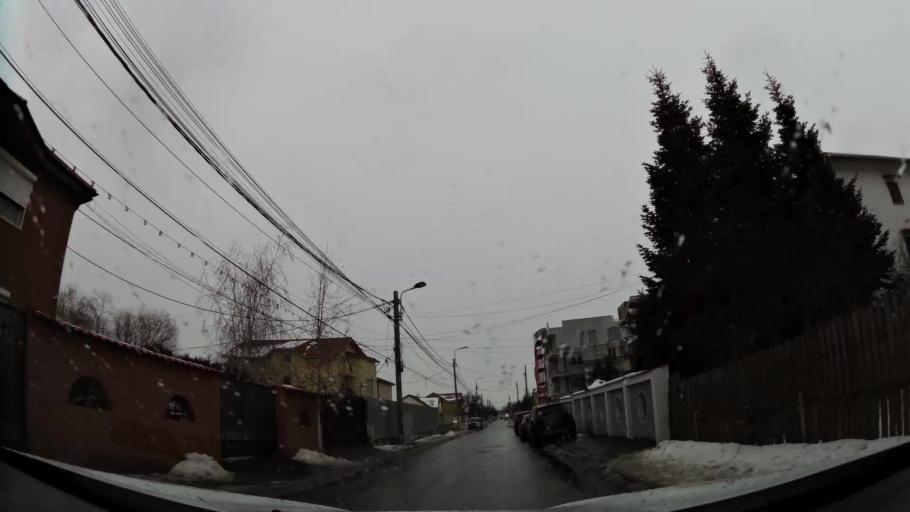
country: RO
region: Ilfov
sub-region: Comuna Chiajna
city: Rosu
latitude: 44.4104
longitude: 26.0105
